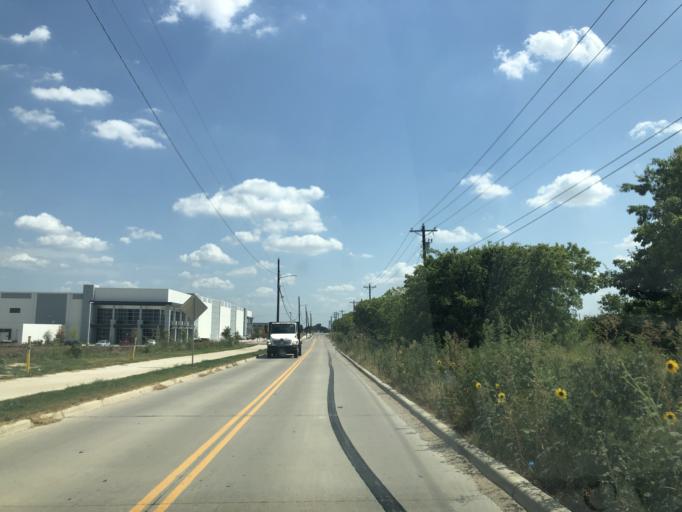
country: US
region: Texas
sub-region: Tarrant County
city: Haslet
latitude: 32.9373
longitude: -97.3228
